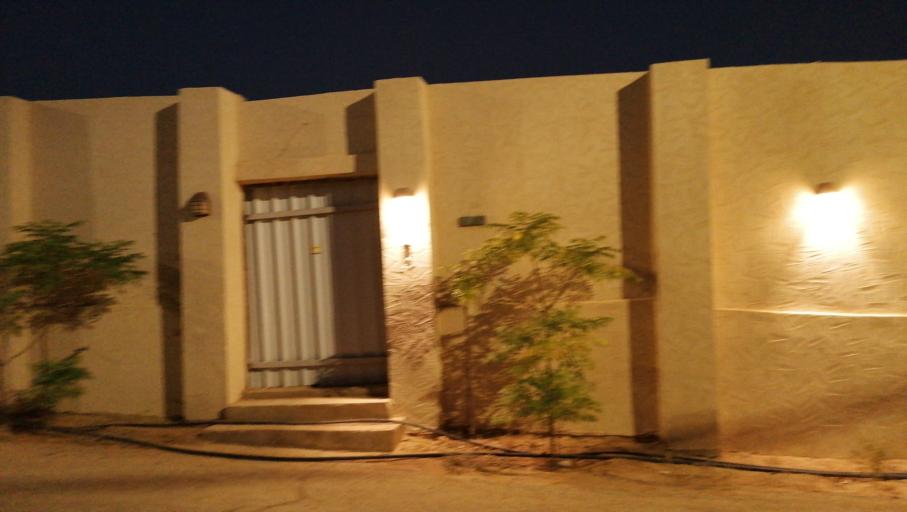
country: SA
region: Al-Qassim
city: Buraydah
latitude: 26.2992
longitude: 43.9188
